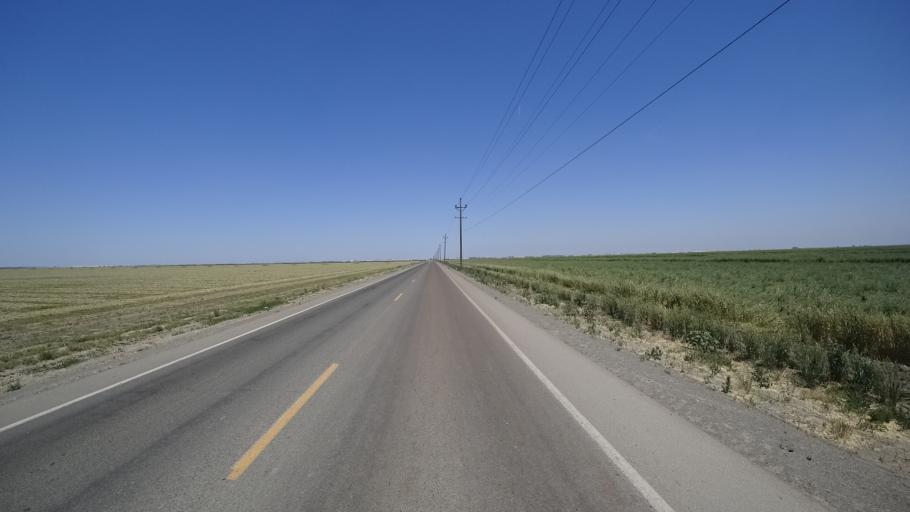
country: US
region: California
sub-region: Kings County
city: Corcoran
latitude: 36.1528
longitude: -119.6458
